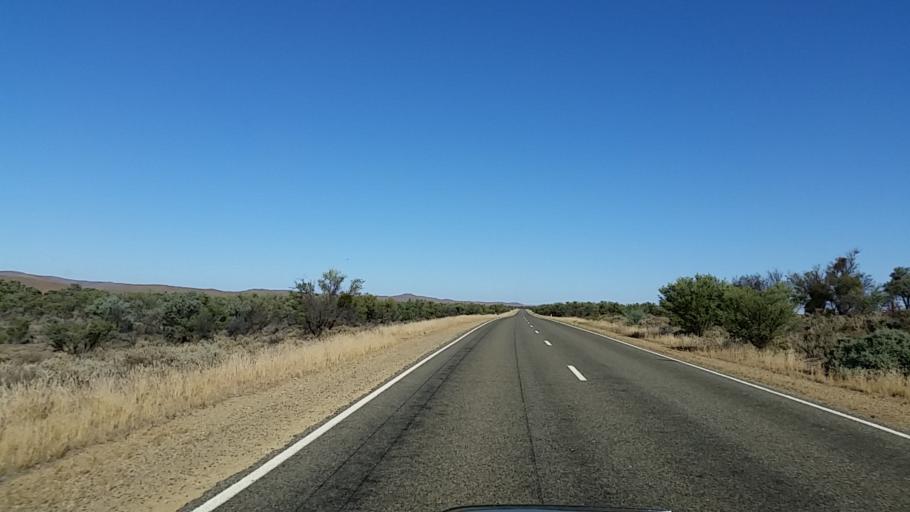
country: AU
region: South Australia
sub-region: Flinders Ranges
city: Quorn
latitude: -32.3941
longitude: 138.5096
